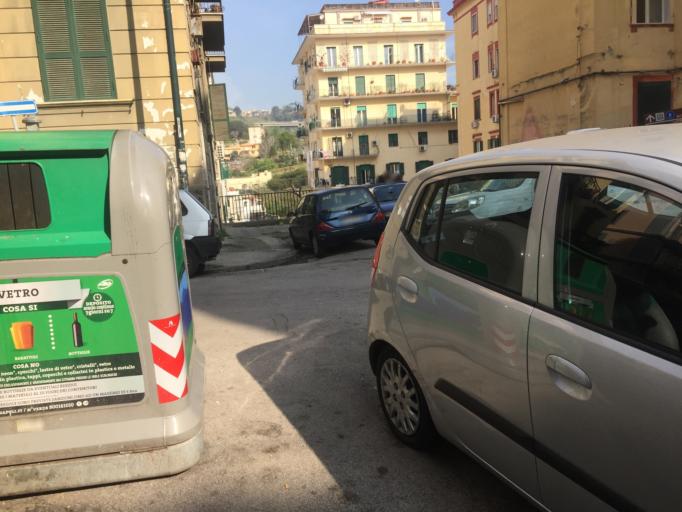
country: IT
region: Campania
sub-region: Provincia di Napoli
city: Napoli
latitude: 40.8576
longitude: 14.2420
